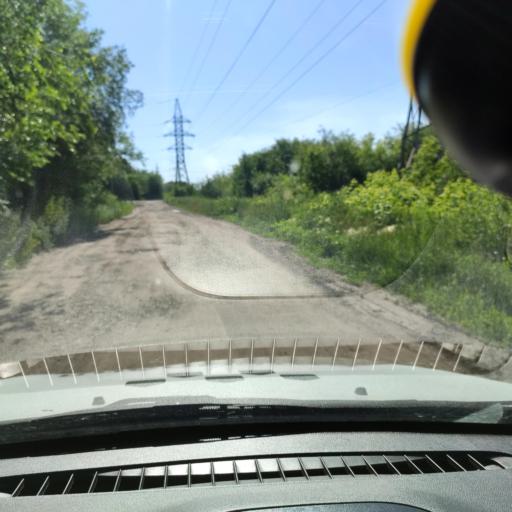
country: RU
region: Samara
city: Tol'yatti
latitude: 53.5832
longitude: 49.2538
